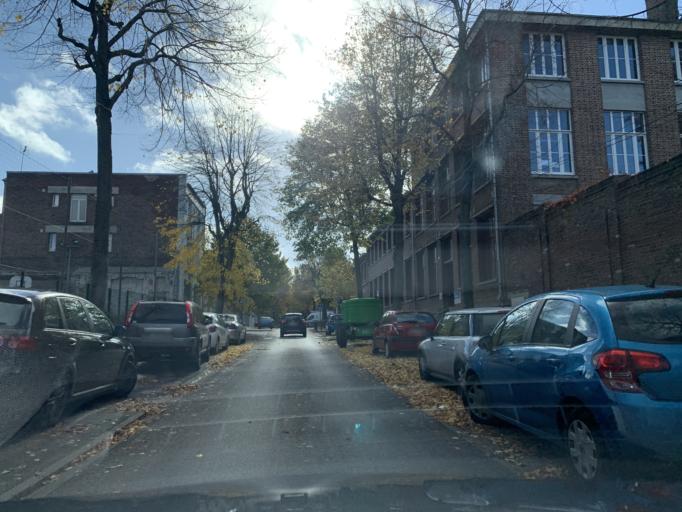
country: FR
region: Nord-Pas-de-Calais
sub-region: Departement du Nord
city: Cambrai
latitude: 50.1805
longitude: 3.2384
